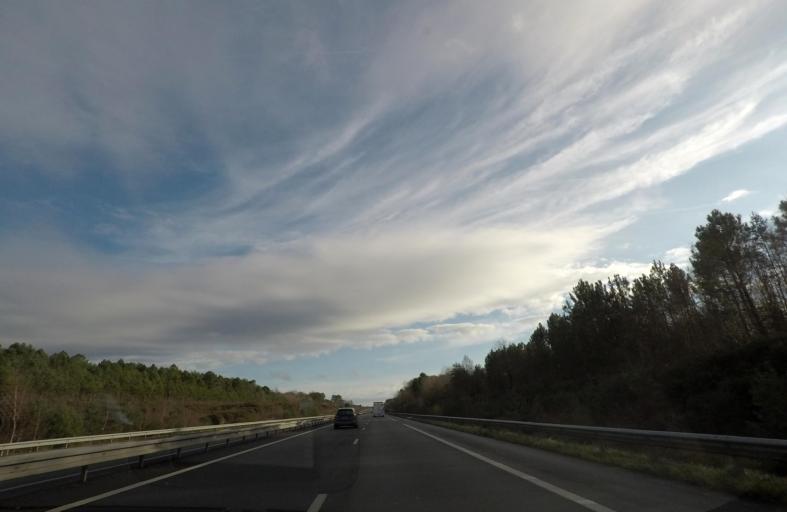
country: FR
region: Centre
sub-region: Departement du Loir-et-Cher
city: Villefranche-sur-Cher
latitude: 47.3147
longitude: 1.8124
